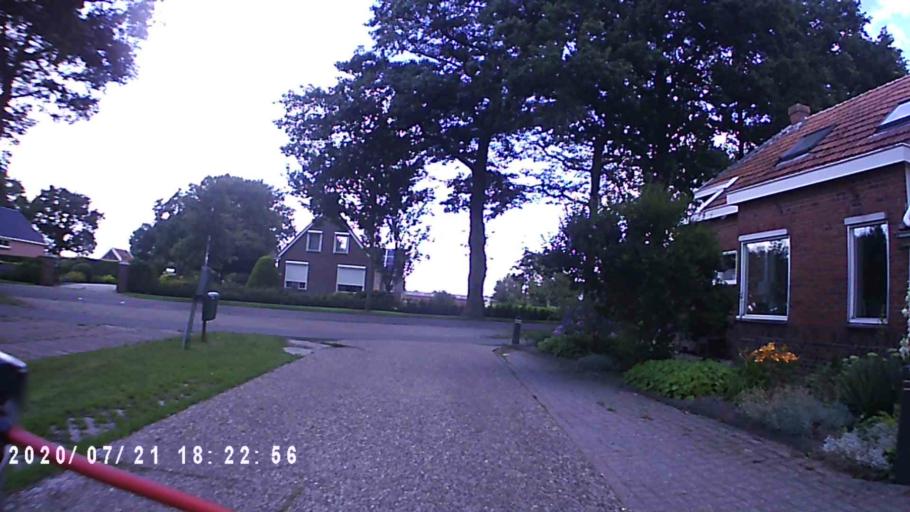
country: NL
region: Groningen
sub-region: Gemeente Hoogezand-Sappemeer
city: Hoogezand
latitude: 53.1874
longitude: 6.7677
